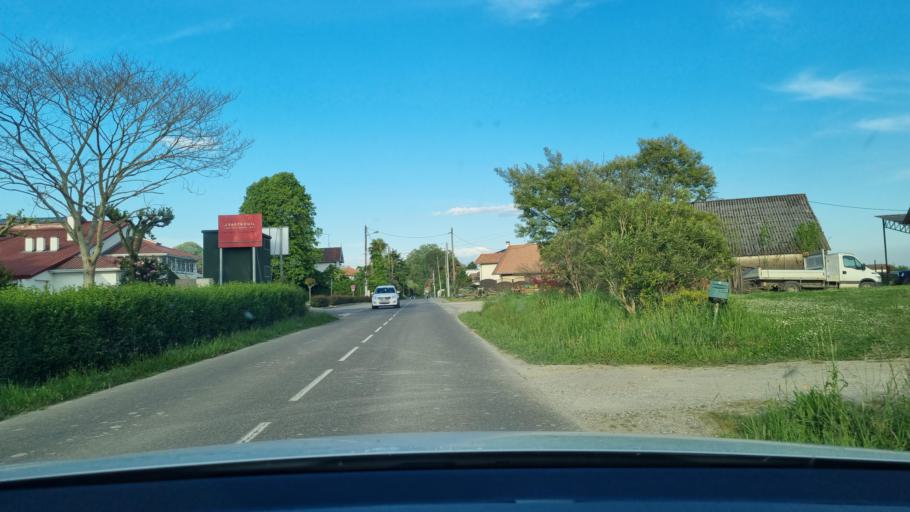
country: FR
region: Aquitaine
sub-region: Departement des Landes
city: Peyrehorade
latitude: 43.5420
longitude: -1.1115
